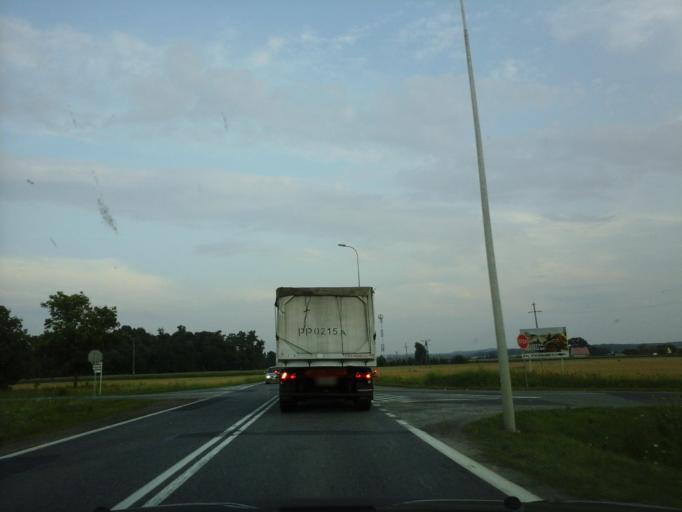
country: PL
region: Lower Silesian Voivodeship
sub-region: Powiat trzebnicki
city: Prusice
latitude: 51.3771
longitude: 16.9490
